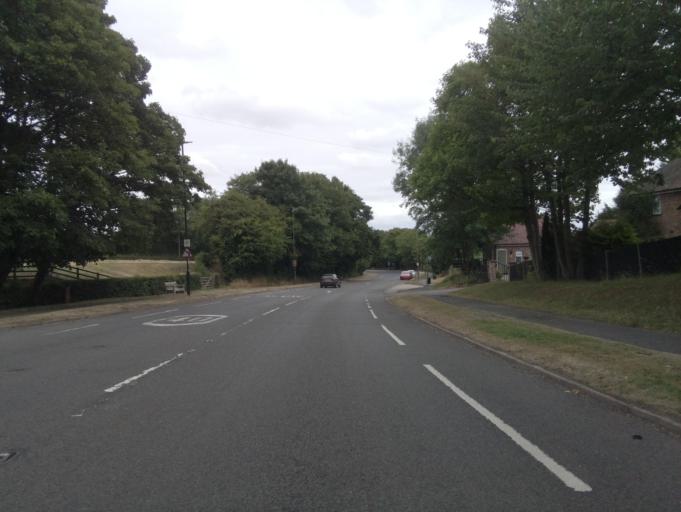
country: GB
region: England
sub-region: Derbyshire
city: Long Eaton
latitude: 52.9169
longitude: -1.3221
